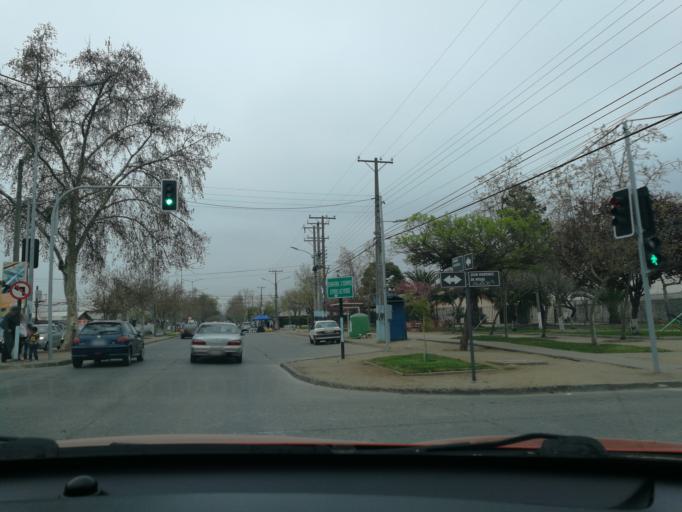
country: CL
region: O'Higgins
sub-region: Provincia de Cachapoal
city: Rancagua
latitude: -34.1627
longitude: -70.7225
